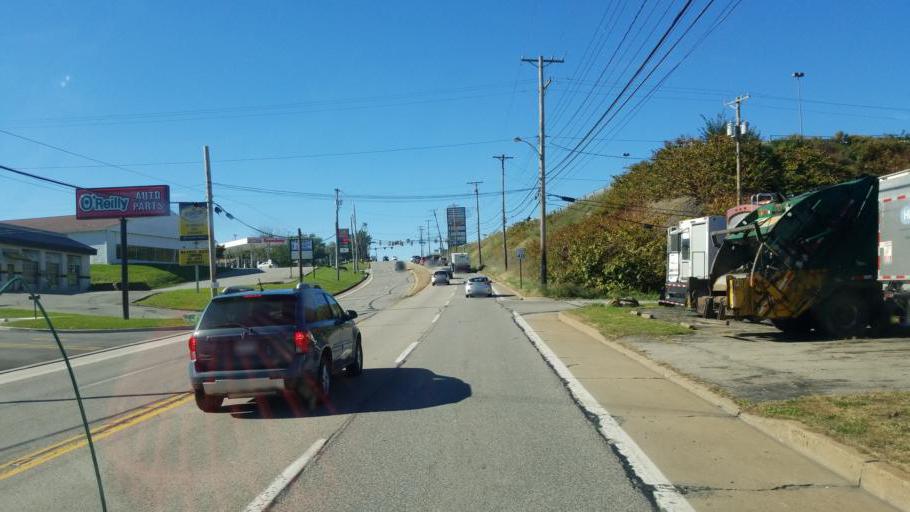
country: US
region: Pennsylvania
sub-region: Allegheny County
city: East McKeesport
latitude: 40.3698
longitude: -79.7840
